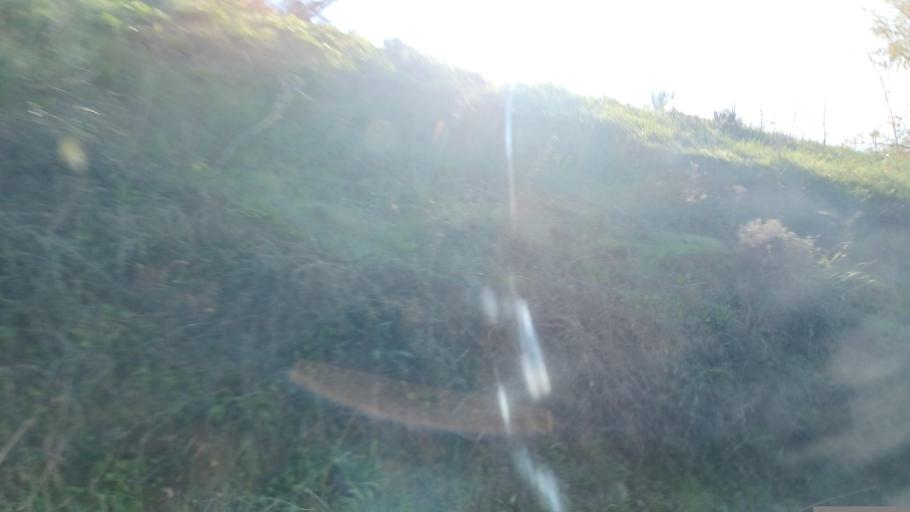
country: CY
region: Pafos
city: Mesogi
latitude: 34.8445
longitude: 32.5201
